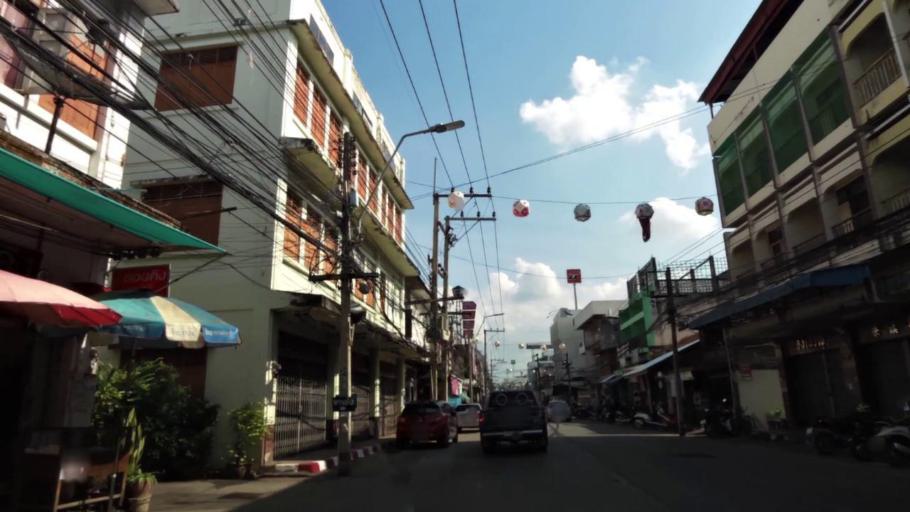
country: TH
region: Phrae
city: Phrae
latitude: 18.1396
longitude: 100.1458
